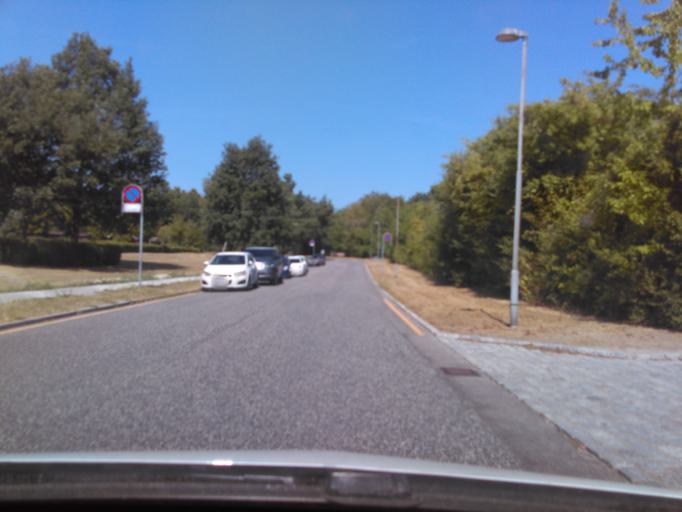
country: DK
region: Capital Region
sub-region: Fureso Kommune
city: Stavnsholt
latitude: 55.8234
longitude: 12.3864
